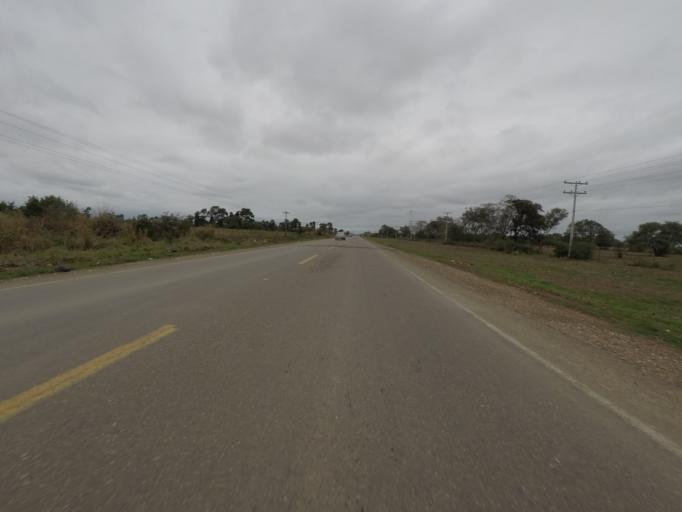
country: BO
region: Santa Cruz
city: Okinawa Numero Uno
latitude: -17.2525
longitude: -62.5554
